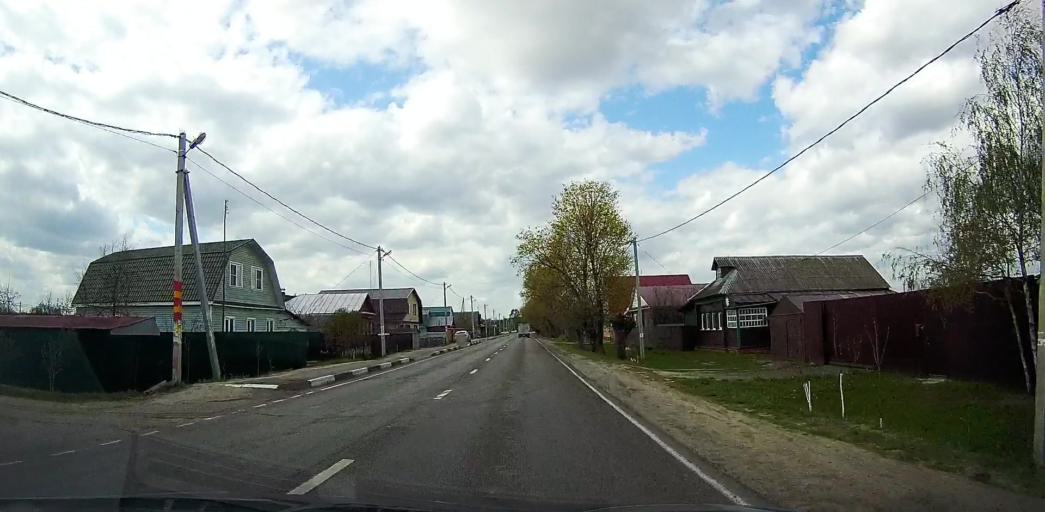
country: RU
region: Moskovskaya
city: Davydovo
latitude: 55.6387
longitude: 38.8648
